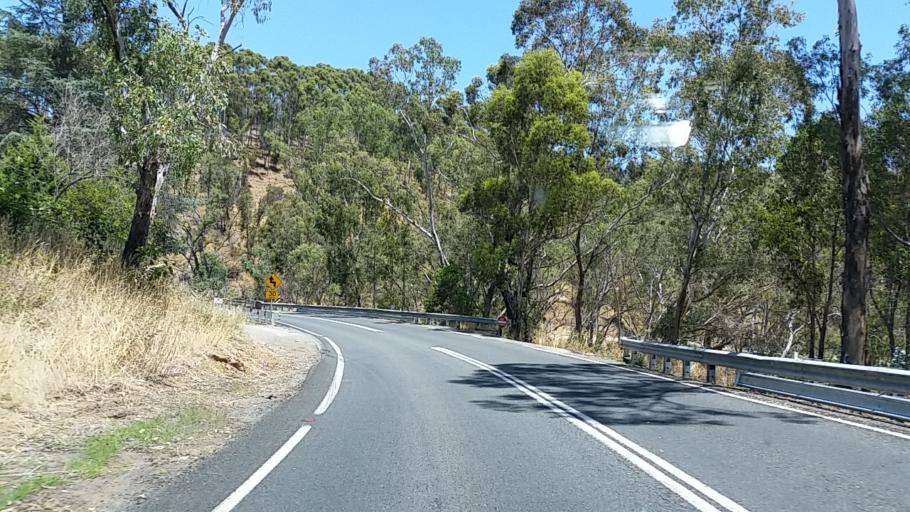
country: AU
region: South Australia
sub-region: Adelaide Hills
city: Gumeracha
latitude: -34.8219
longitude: 138.8518
